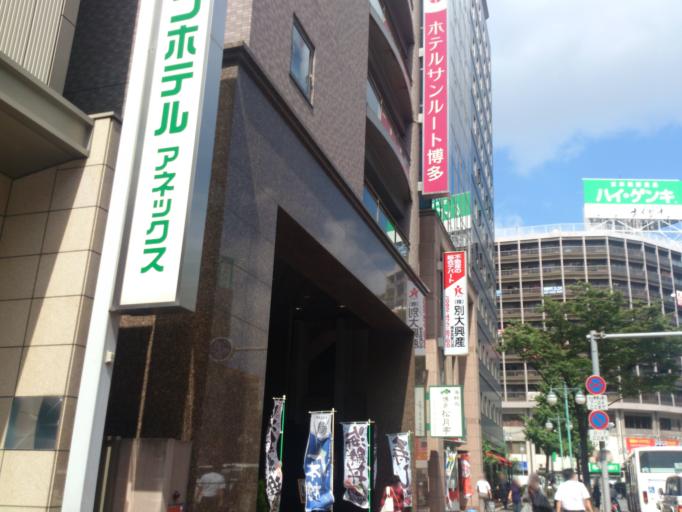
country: JP
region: Fukuoka
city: Fukuoka-shi
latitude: 33.5912
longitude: 130.4226
